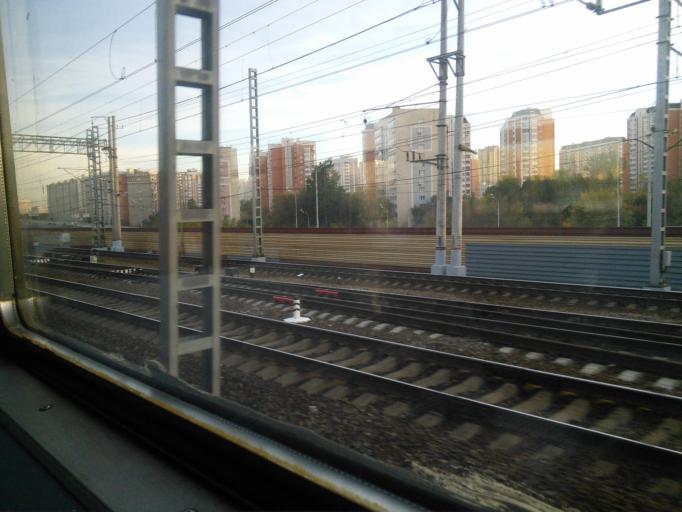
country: RU
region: Moscow
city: Businovo
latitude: 55.8758
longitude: 37.4952
